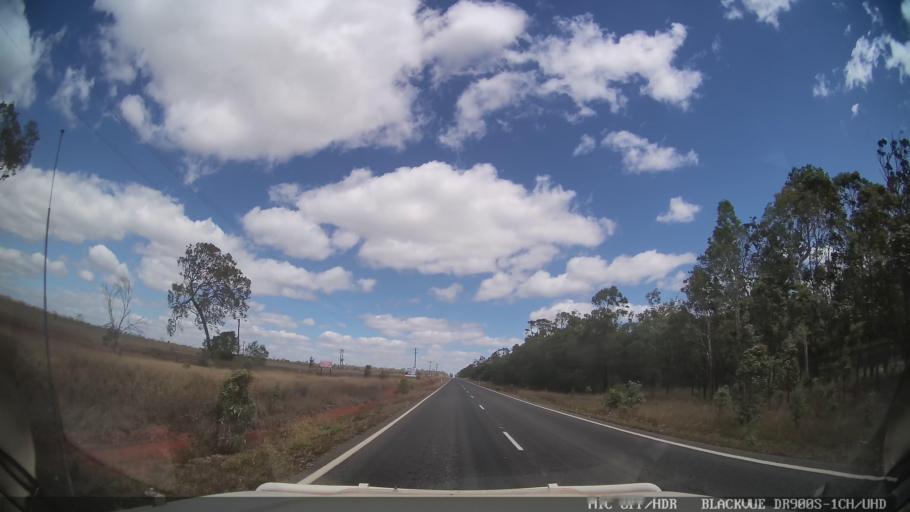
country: AU
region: Queensland
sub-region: Tablelands
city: Ravenshoe
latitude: -18.0360
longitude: 144.8693
